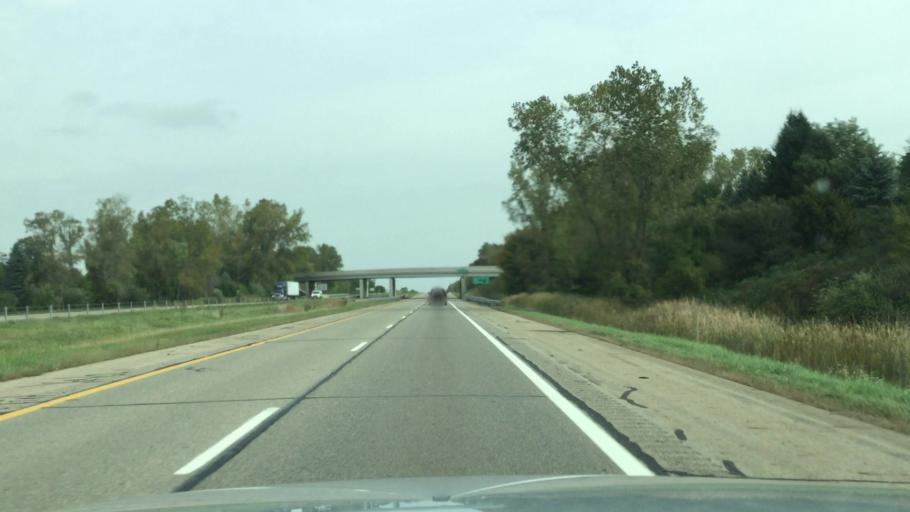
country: US
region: Michigan
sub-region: Shiawassee County
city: Durand
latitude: 42.9329
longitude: -83.9900
